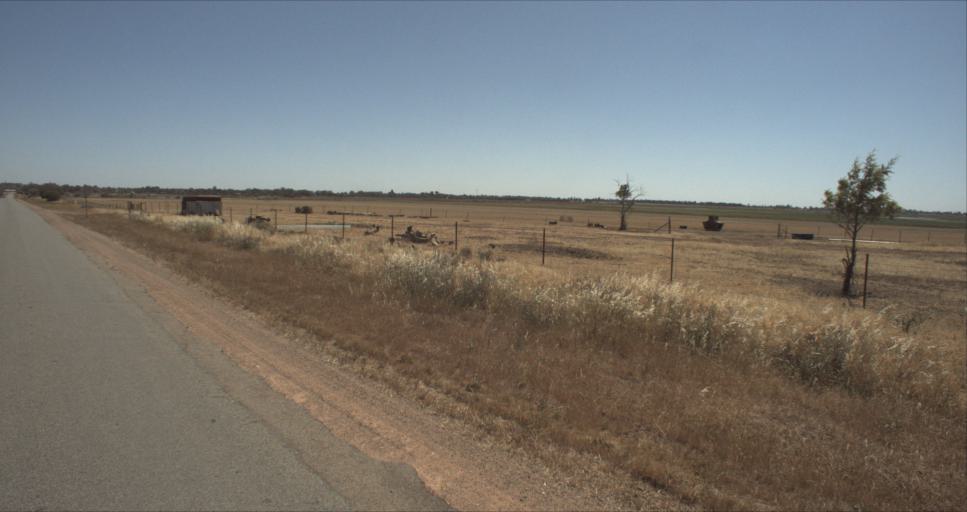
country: AU
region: New South Wales
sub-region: Leeton
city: Leeton
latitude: -34.5400
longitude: 146.4402
